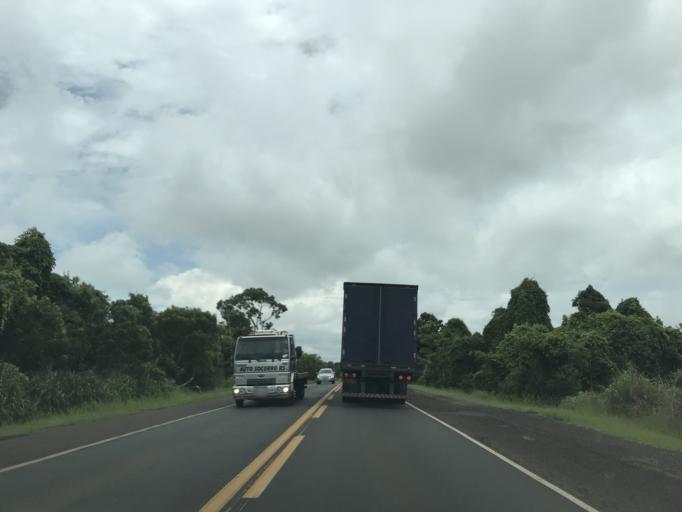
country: BR
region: Minas Gerais
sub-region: Frutal
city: Frutal
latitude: -19.7746
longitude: -48.9652
